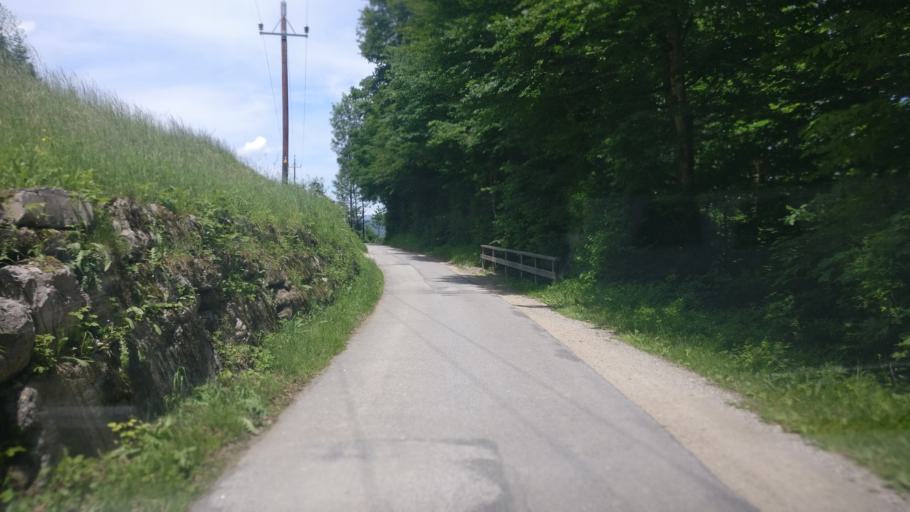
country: AT
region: Salzburg
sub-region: Politischer Bezirk Hallein
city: Hallein
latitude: 47.6596
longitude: 13.1150
